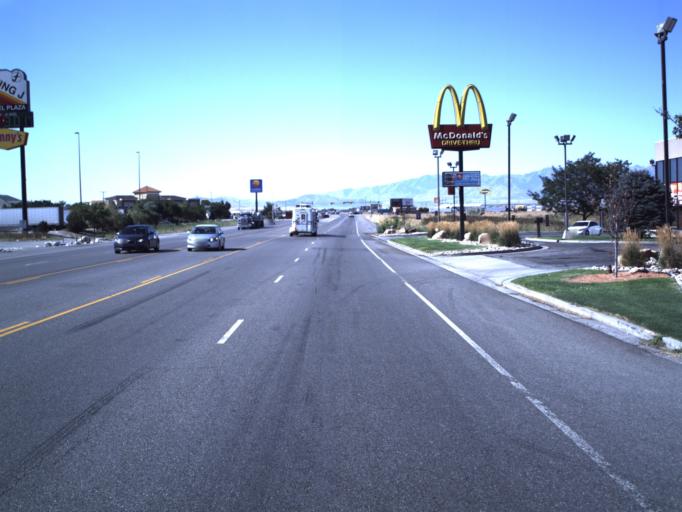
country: US
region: Utah
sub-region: Tooele County
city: Stansbury park
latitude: 40.6888
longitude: -112.2658
